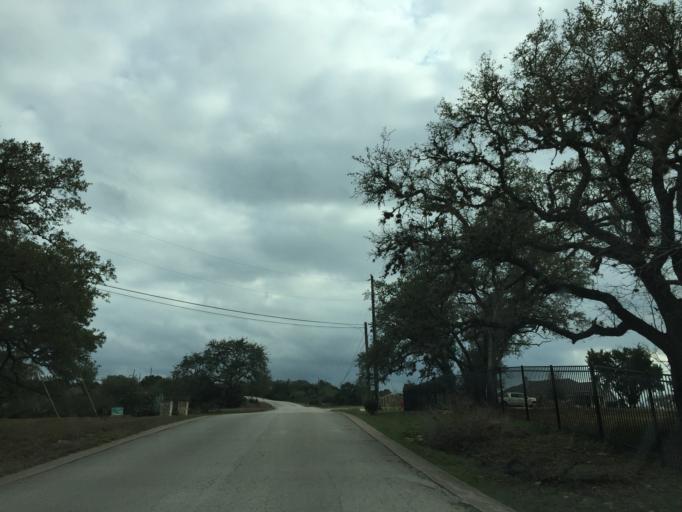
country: US
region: Texas
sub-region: Travis County
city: Shady Hollow
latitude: 30.1497
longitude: -97.9722
